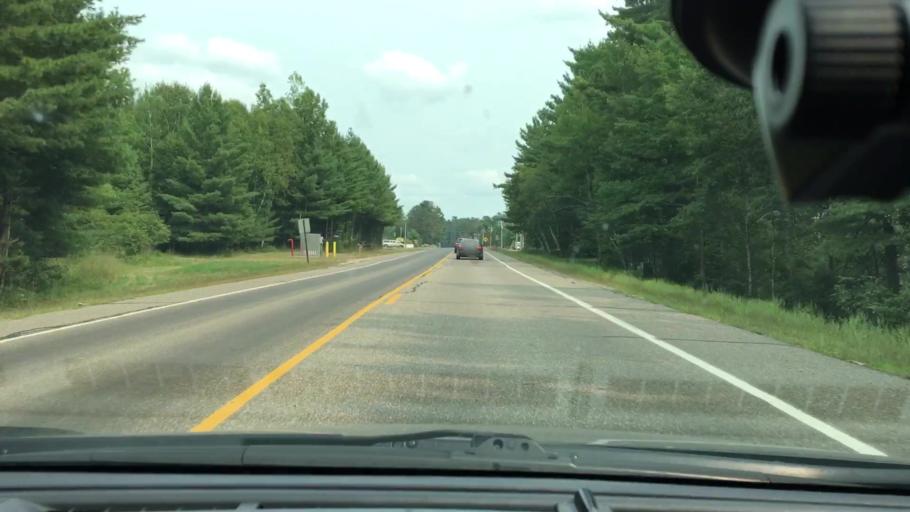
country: US
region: Minnesota
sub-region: Crow Wing County
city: Cross Lake
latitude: 46.7308
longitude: -93.9687
